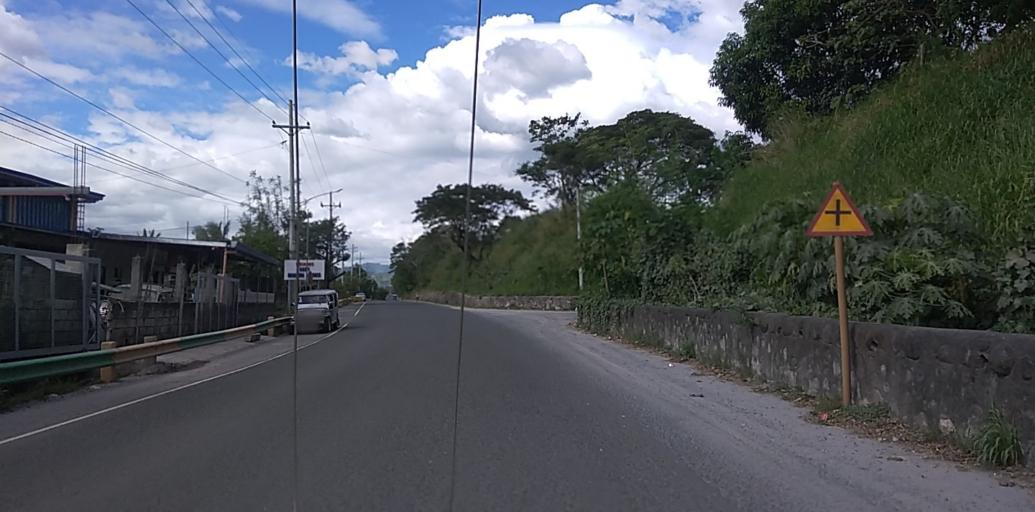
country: PH
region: Central Luzon
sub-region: Province of Pampanga
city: Dolores
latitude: 15.0920
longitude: 120.5345
